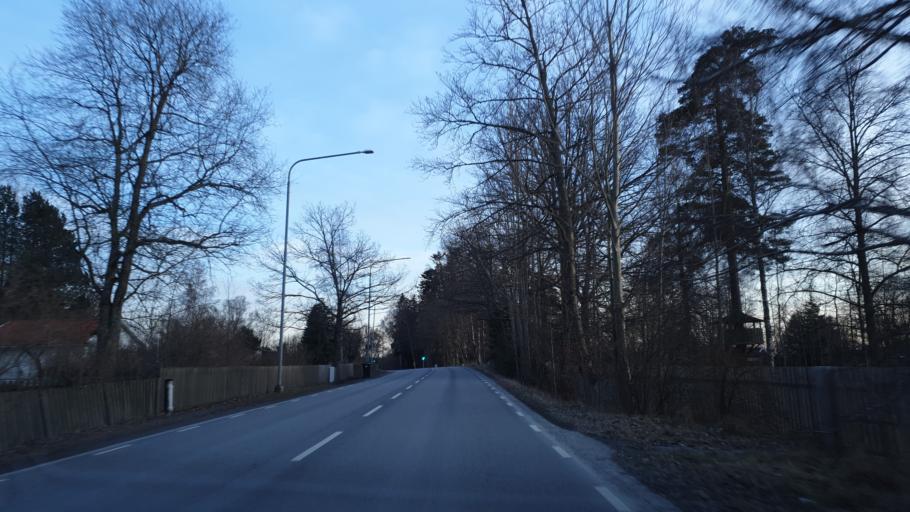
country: SE
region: Uppsala
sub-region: Habo Kommun
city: Balsta
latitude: 59.5569
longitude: 17.5455
